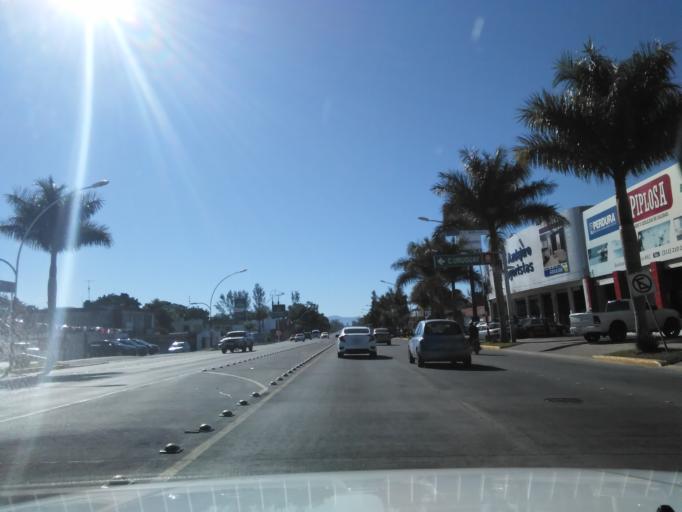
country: MX
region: Nayarit
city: Tepic
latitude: 21.4834
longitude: -104.8930
